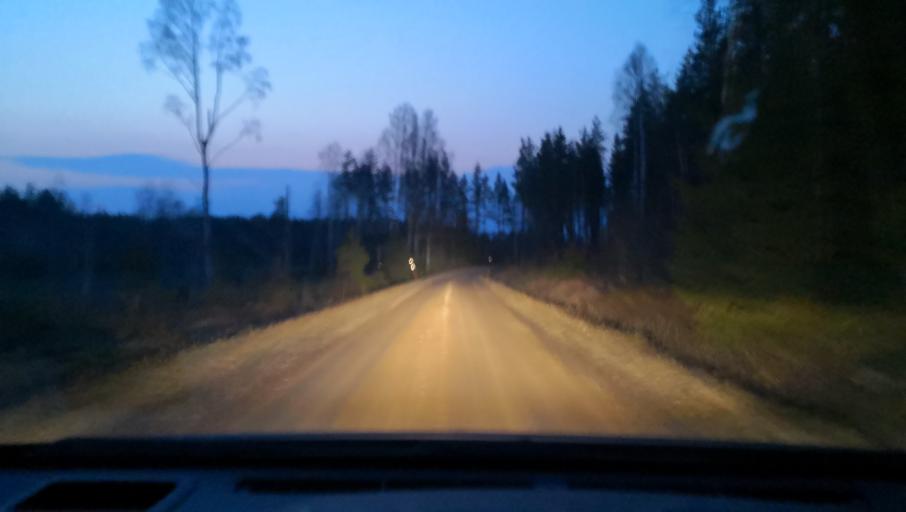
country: SE
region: OErebro
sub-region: Lindesbergs Kommun
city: Frovi
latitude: 59.5960
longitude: 15.4676
